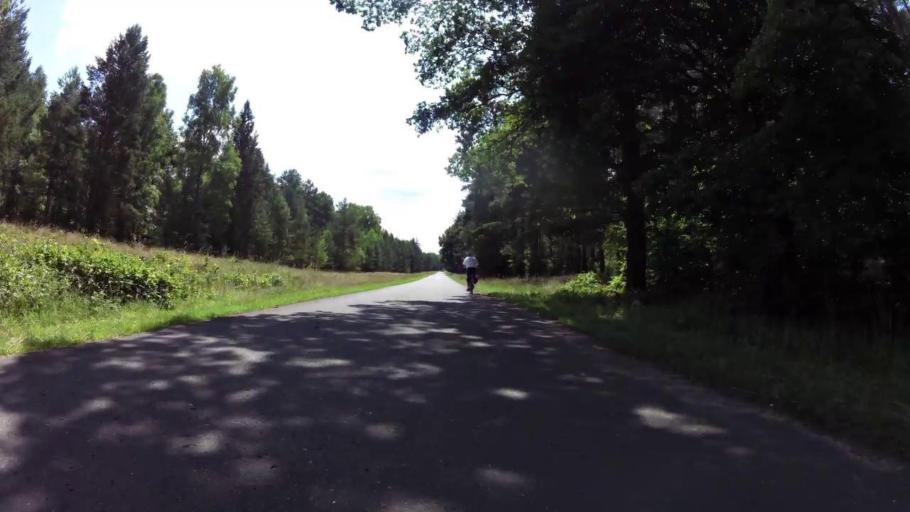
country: PL
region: West Pomeranian Voivodeship
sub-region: Powiat choszczenski
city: Drawno
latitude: 53.3835
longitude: 15.7289
